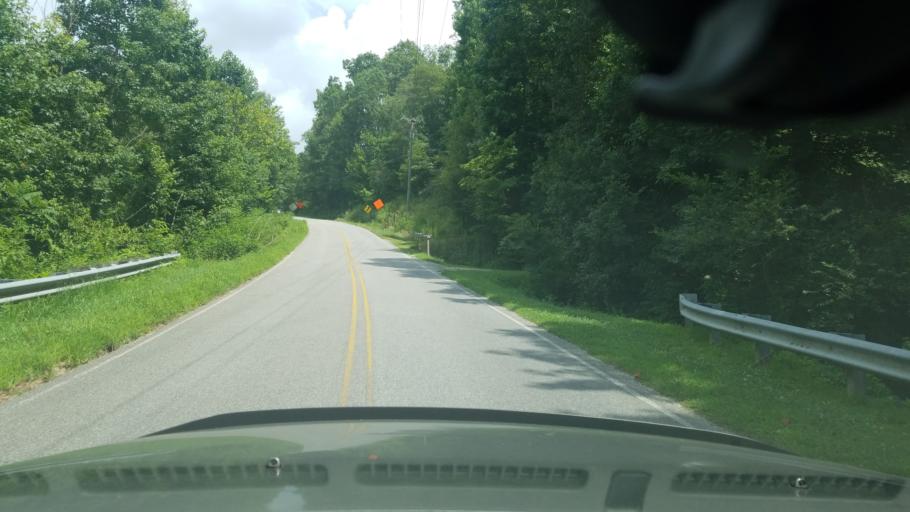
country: US
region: Georgia
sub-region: Forsyth County
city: Cumming
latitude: 34.2719
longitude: -84.2233
